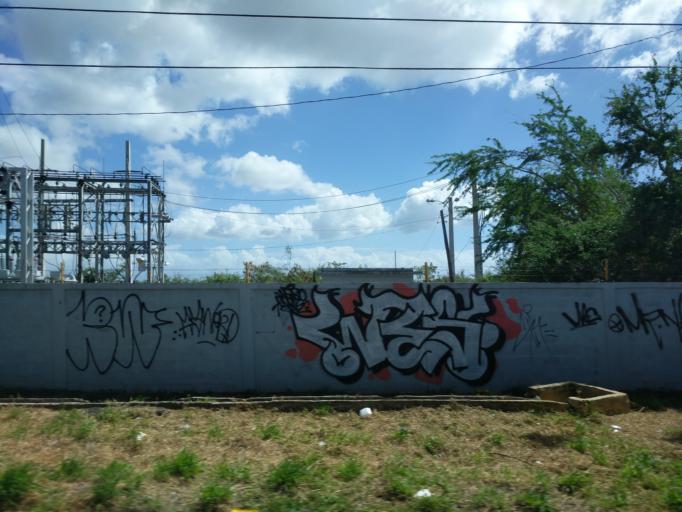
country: PR
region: Santa Isabel Municipio
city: El Ojo
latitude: 18.0171
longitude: -66.3734
